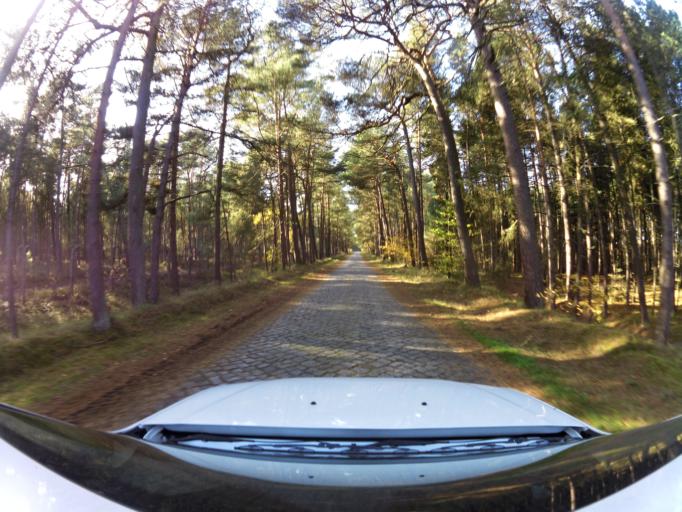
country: PL
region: West Pomeranian Voivodeship
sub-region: Powiat gryficki
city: Trzebiatow
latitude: 54.1158
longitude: 15.1672
